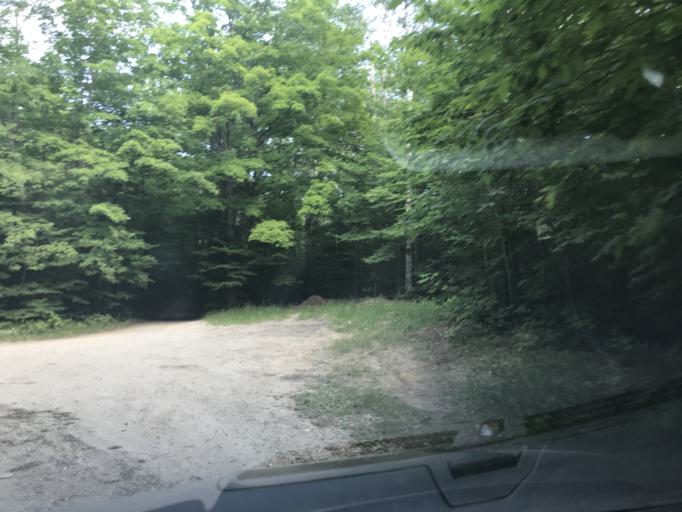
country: US
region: Michigan
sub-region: Cheboygan County
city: Indian River
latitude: 45.5927
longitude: -84.6716
